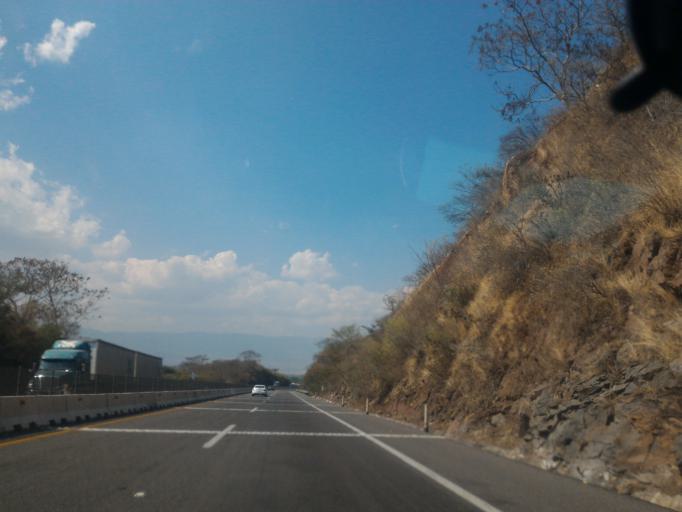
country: MX
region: Jalisco
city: Usmajac
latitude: 19.8679
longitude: -103.5100
